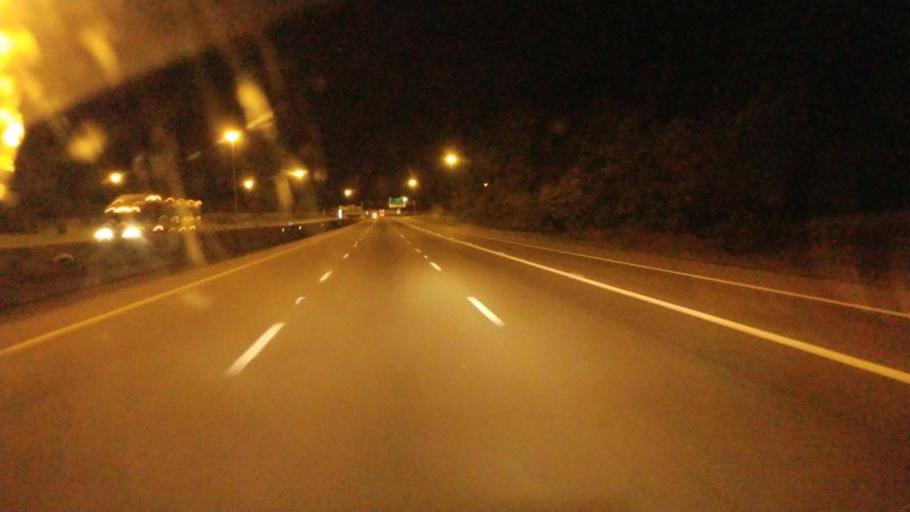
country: US
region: Ohio
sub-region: Montgomery County
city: Vandalia
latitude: 39.8647
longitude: -84.2146
